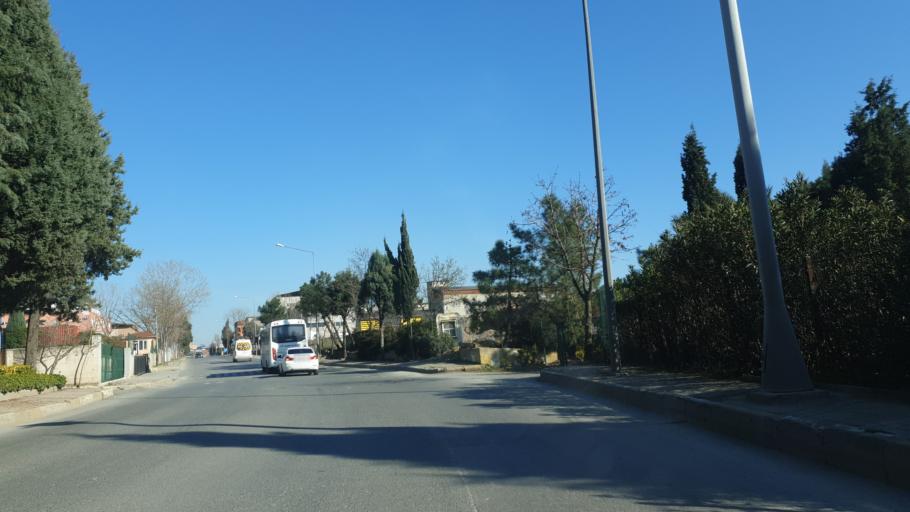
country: TR
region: Istanbul
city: Icmeler
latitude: 40.8788
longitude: 29.3590
